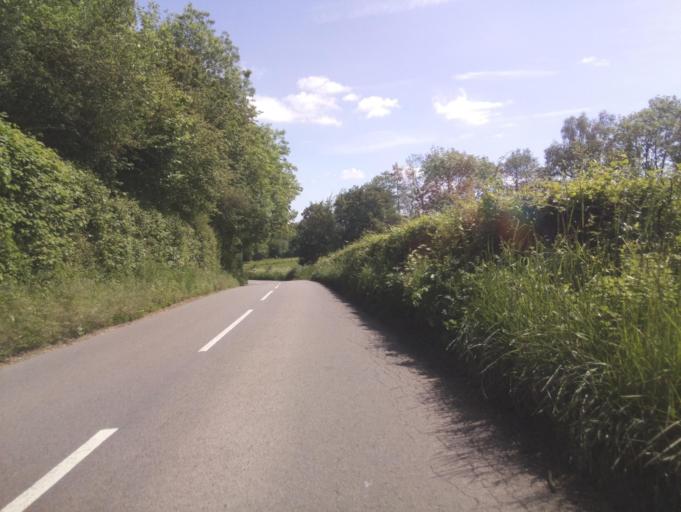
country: GB
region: England
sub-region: Herefordshire
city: Llanrothal
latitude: 51.8443
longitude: -2.7806
